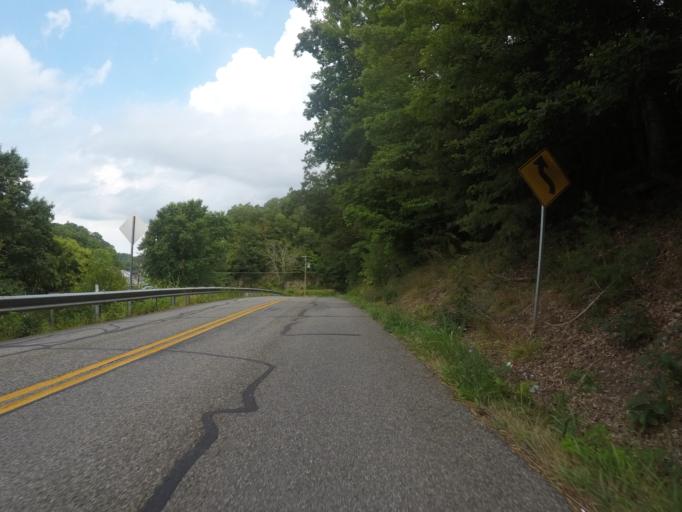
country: US
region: Kentucky
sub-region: Boyd County
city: Meads
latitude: 38.4103
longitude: -82.6687
